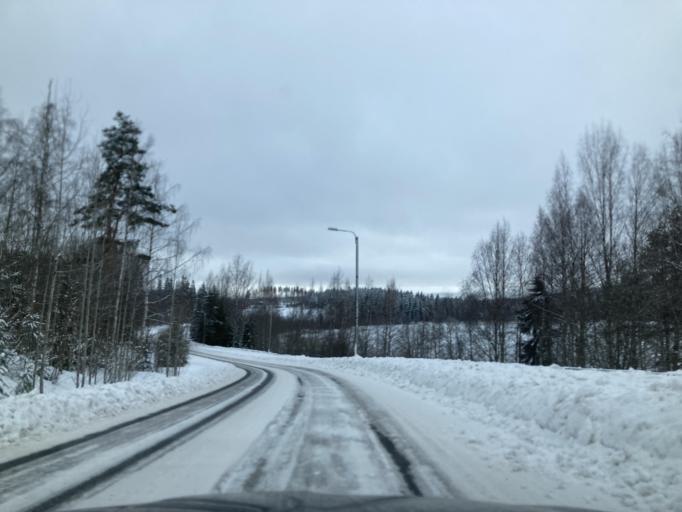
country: FI
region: Central Finland
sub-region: Jaemsae
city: Jaemsae
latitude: 61.8745
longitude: 25.2709
